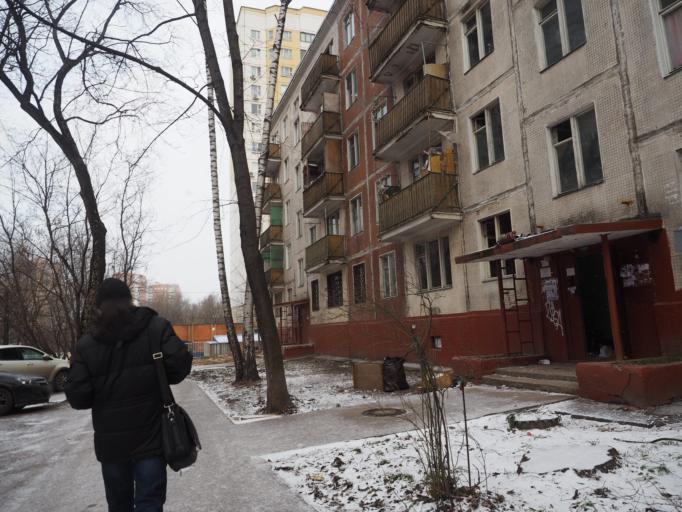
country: RU
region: Moscow
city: Davydkovo
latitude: 55.7309
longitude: 37.4582
